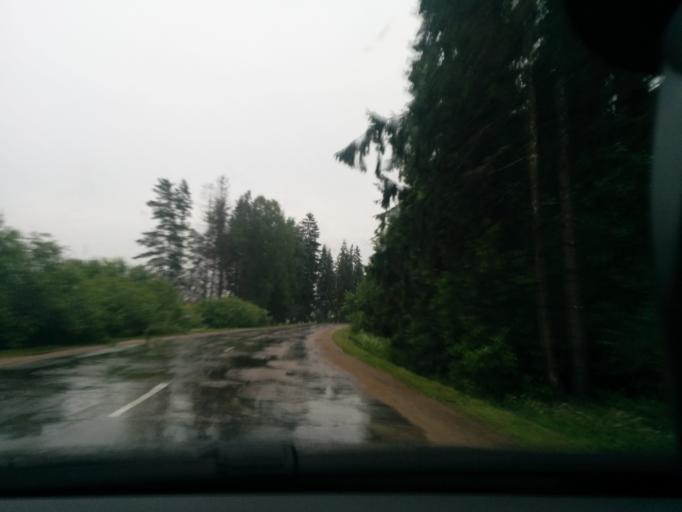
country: LV
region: Ogre
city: Ogre
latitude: 56.8270
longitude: 24.5970
